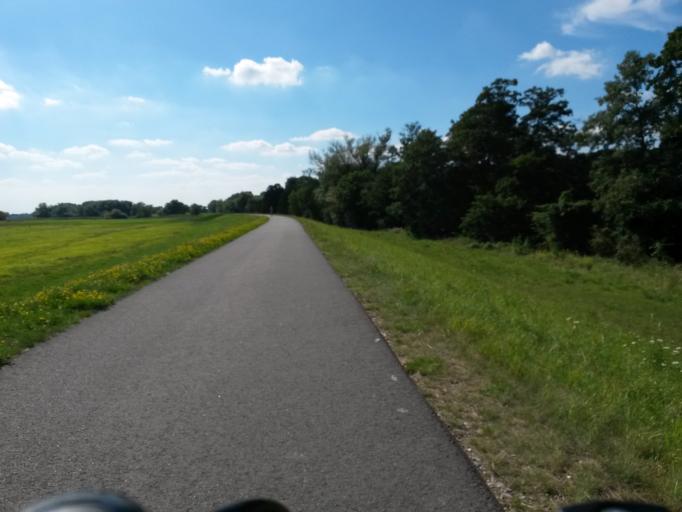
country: DE
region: Brandenburg
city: Meyenburg
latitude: 53.0081
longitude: 14.2223
